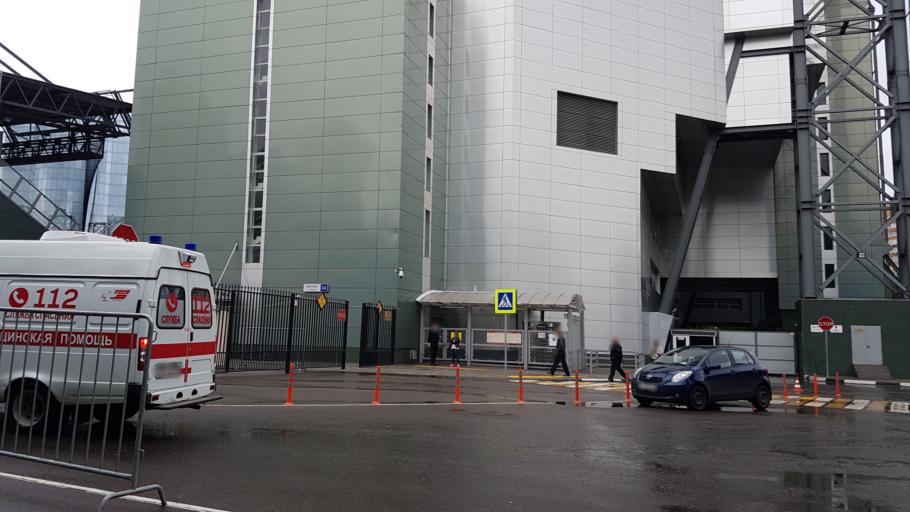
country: RU
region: Moscow
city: Khimki
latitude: 55.8866
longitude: 37.4542
